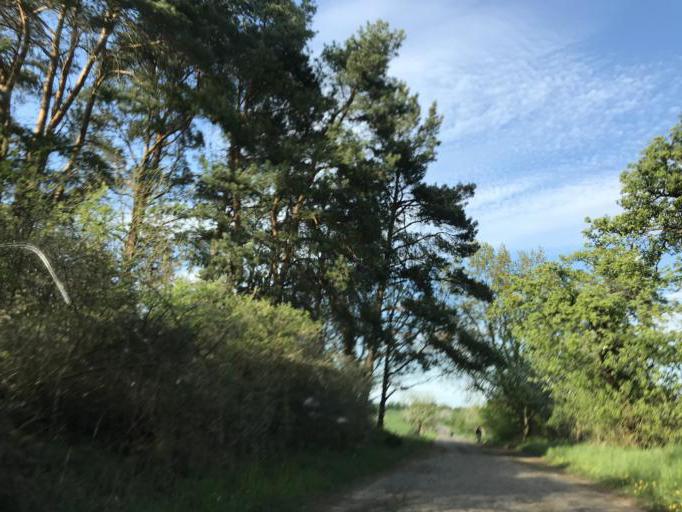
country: DE
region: Brandenburg
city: Joachimsthal
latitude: 52.9726
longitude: 13.7242
